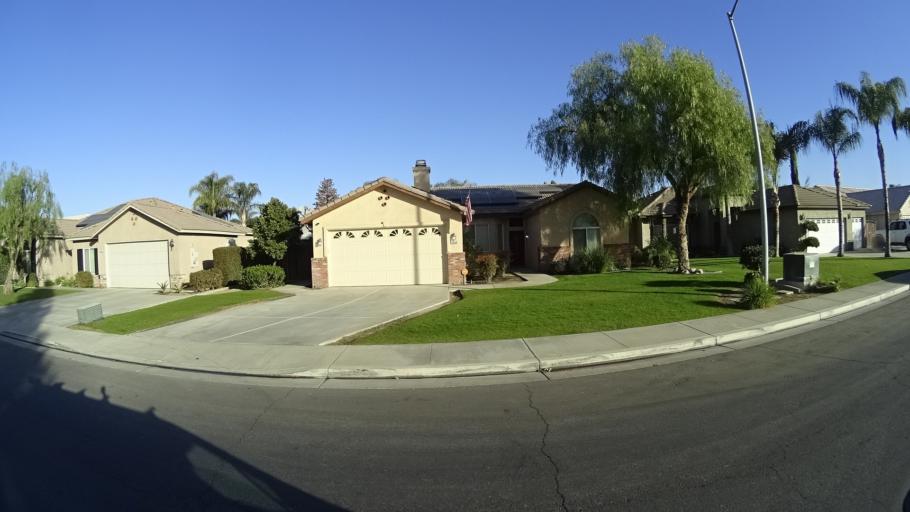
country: US
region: California
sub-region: Kern County
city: Greenfield
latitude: 35.2764
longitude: -119.0359
